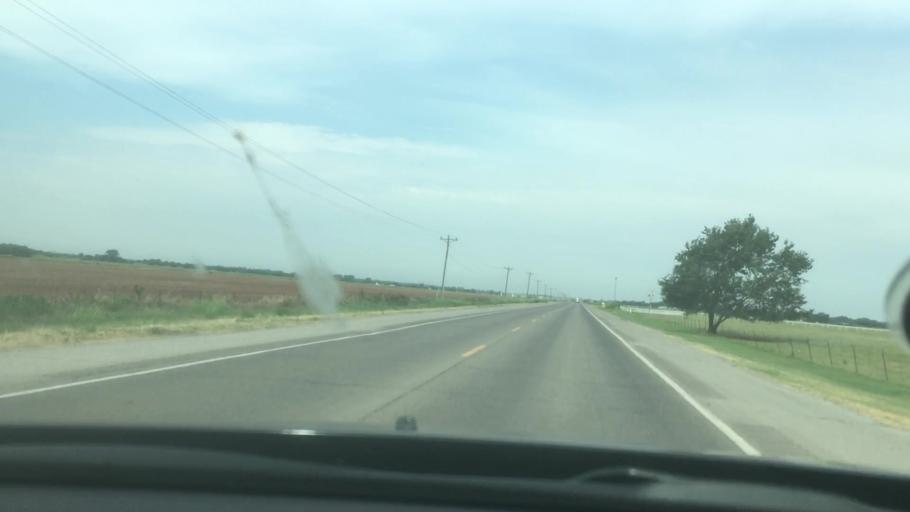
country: US
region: Oklahoma
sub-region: Garvin County
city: Maysville
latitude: 34.8215
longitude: -97.4982
